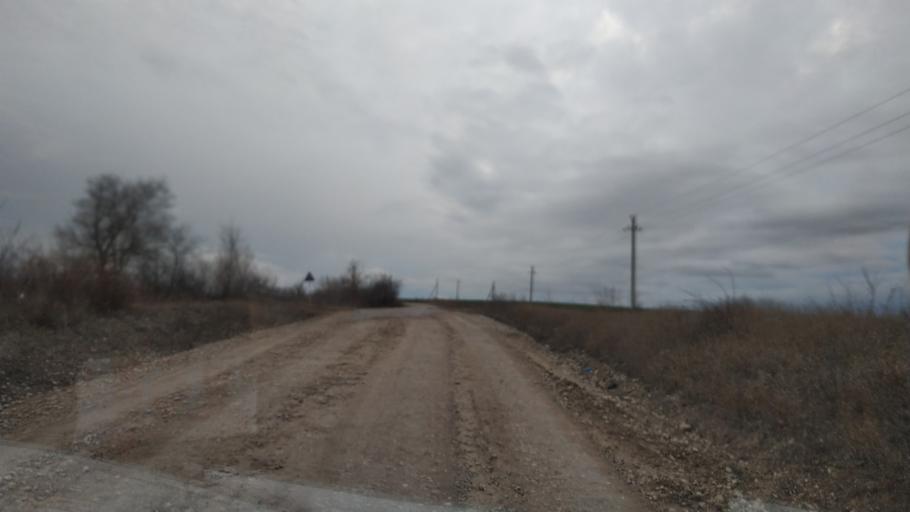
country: MD
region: Causeni
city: Causeni
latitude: 46.6250
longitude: 29.3958
